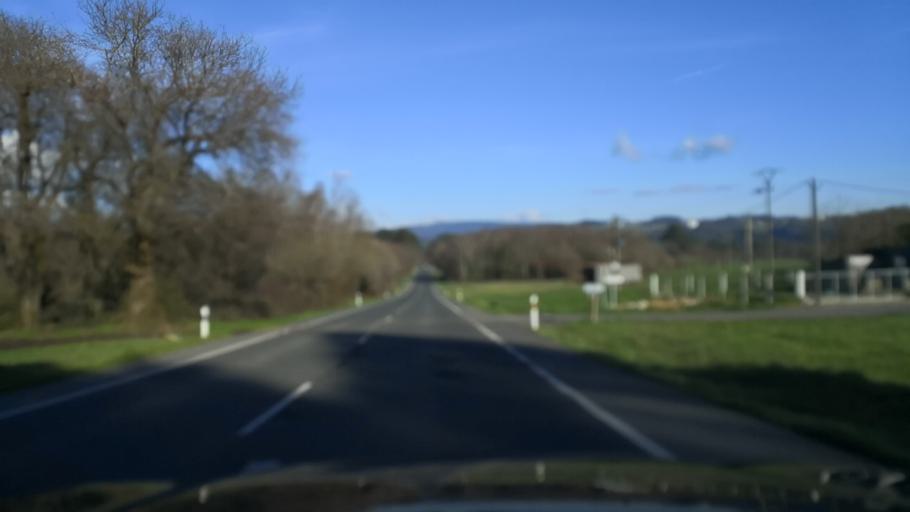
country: ES
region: Galicia
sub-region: Provincia de Pontevedra
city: Silleda
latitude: 42.7058
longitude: -8.3052
